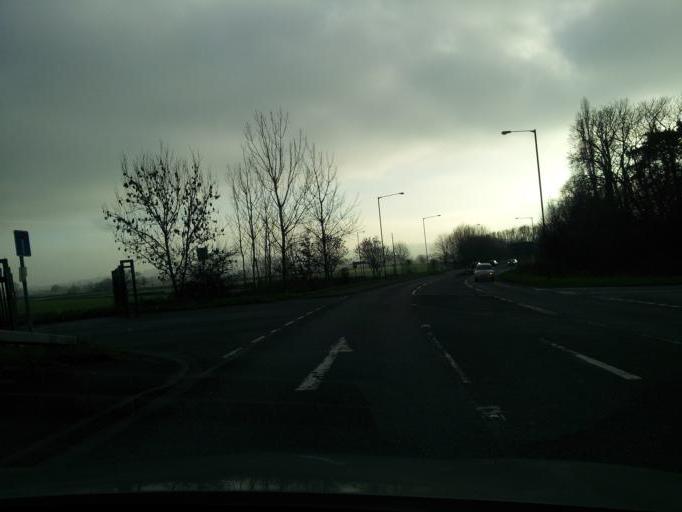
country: GB
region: England
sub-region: Derbyshire
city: Rodsley
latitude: 52.8829
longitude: -1.7533
